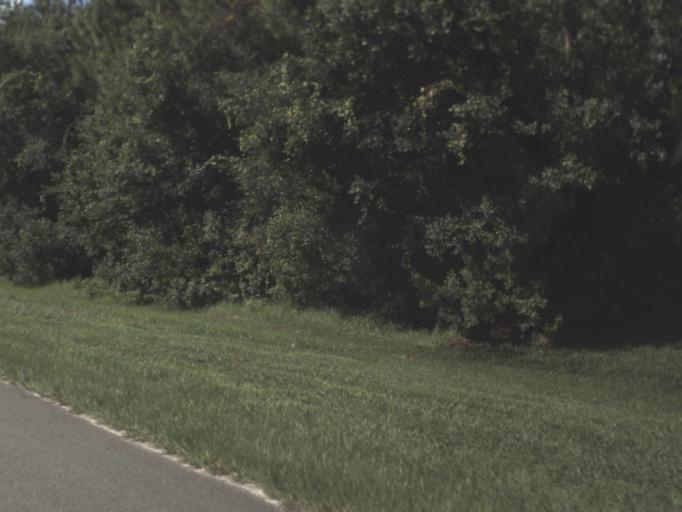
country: US
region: Florida
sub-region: Sarasota County
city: The Meadows
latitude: 27.4118
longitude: -82.3409
